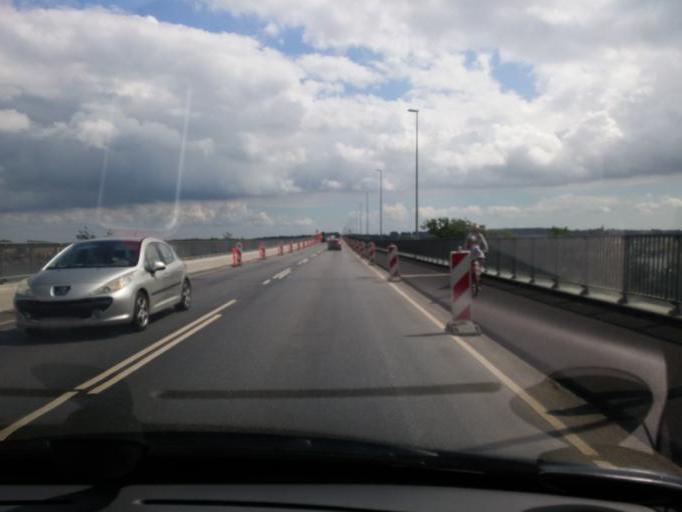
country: DK
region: South Denmark
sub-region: Svendborg Kommune
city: Svendborg
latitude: 55.0509
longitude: 10.5979
